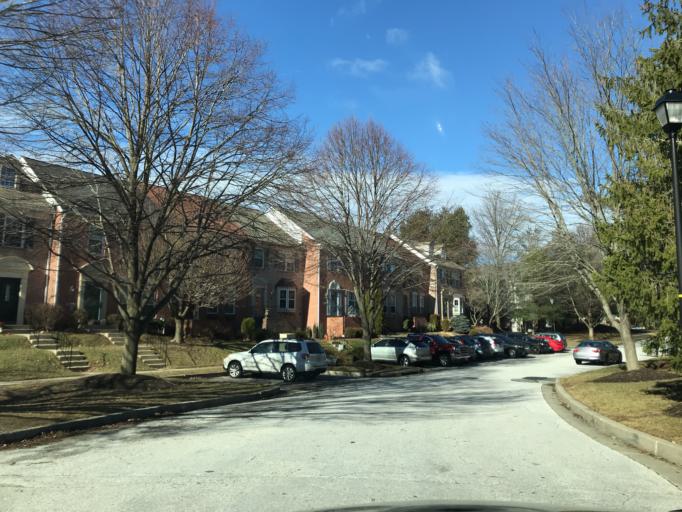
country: US
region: Maryland
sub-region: Baltimore County
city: Carney
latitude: 39.4070
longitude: -76.5463
